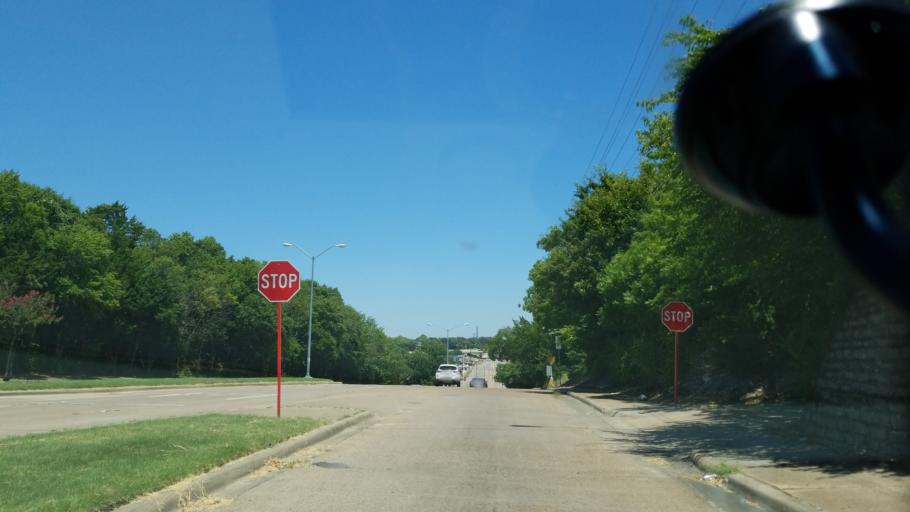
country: US
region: Texas
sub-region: Dallas County
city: Cockrell Hill
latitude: 32.6927
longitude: -96.8399
